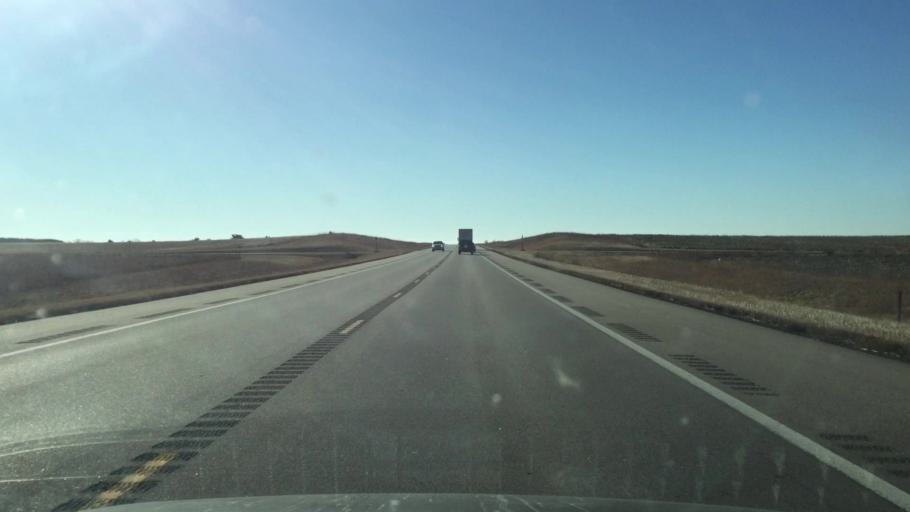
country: US
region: Kansas
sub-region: Allen County
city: Iola
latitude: 38.0547
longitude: -95.3803
